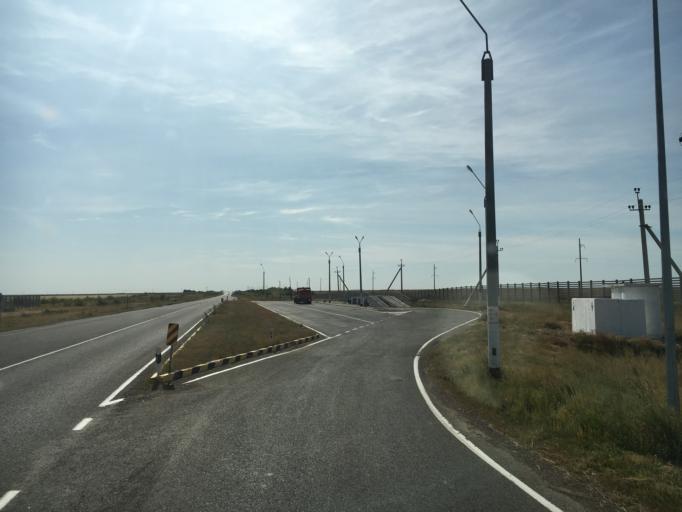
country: KZ
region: Batys Qazaqstan
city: Peremetnoe
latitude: 51.1335
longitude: 50.9024
